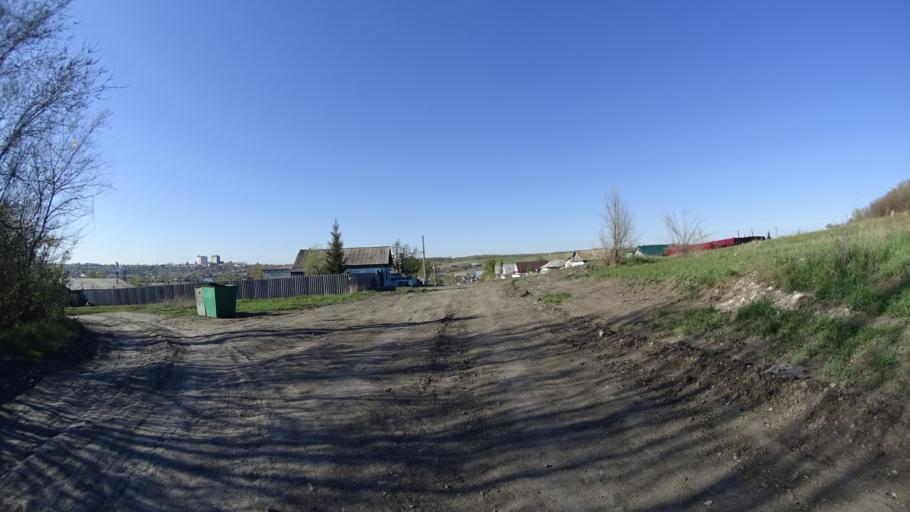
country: RU
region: Chelyabinsk
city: Troitsk
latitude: 54.0896
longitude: 61.6000
